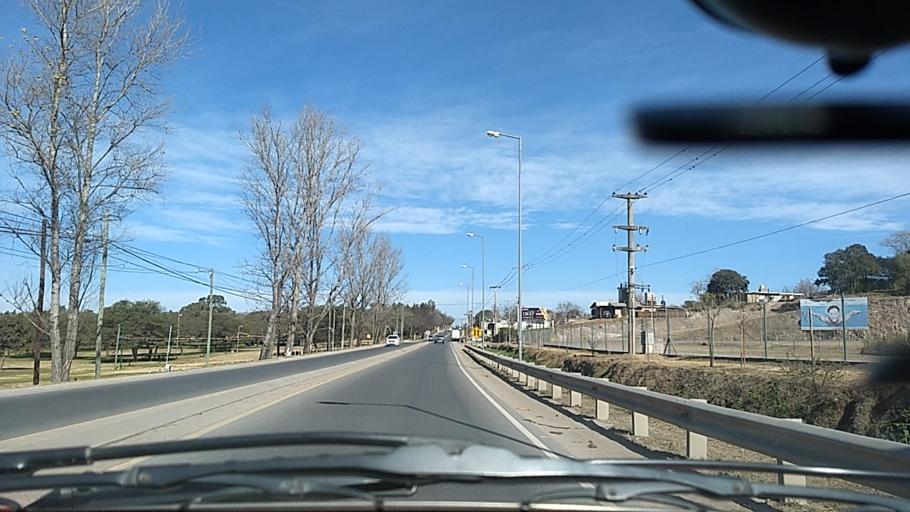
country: AR
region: Cordoba
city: Salsipuedes
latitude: -31.1276
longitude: -64.2946
